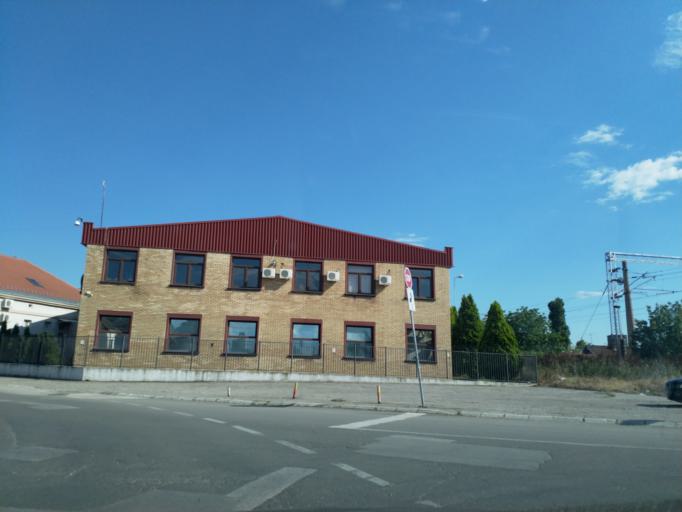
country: RS
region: Central Serbia
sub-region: Pomoravski Okrug
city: Paracin
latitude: 43.8616
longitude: 21.4017
